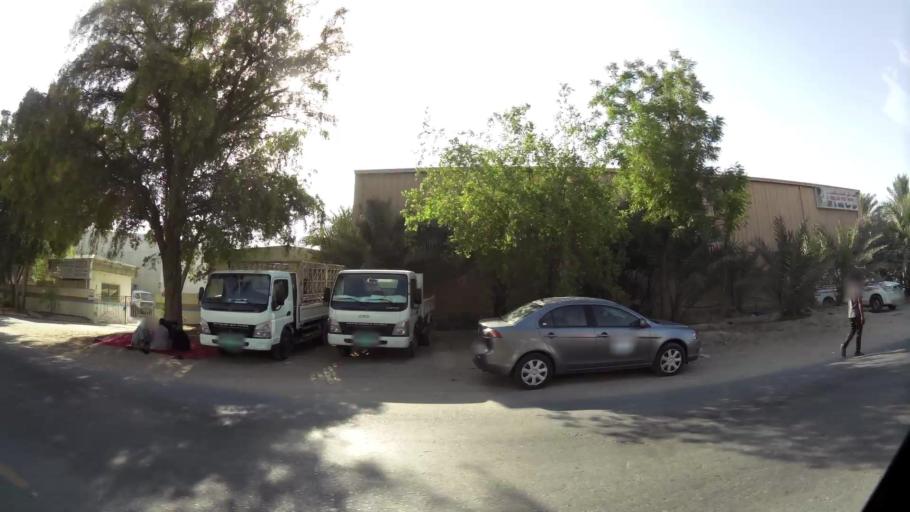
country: AE
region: Dubai
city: Dubai
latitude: 25.1199
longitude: 55.2301
